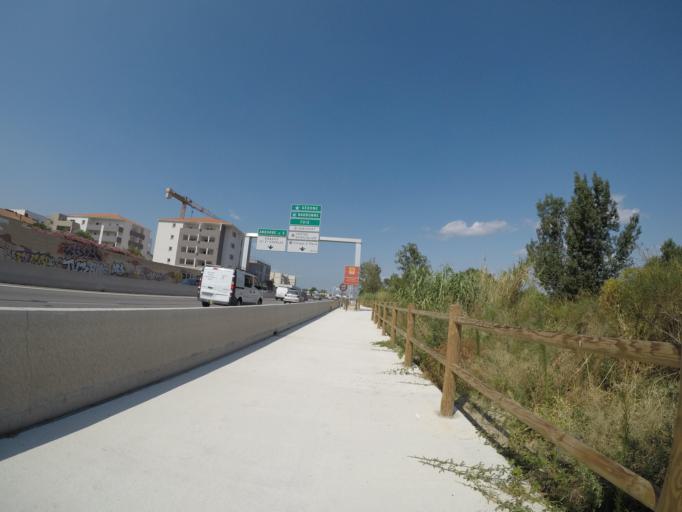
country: FR
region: Languedoc-Roussillon
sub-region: Departement des Pyrenees-Orientales
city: Perpignan
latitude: 42.6987
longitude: 2.8708
